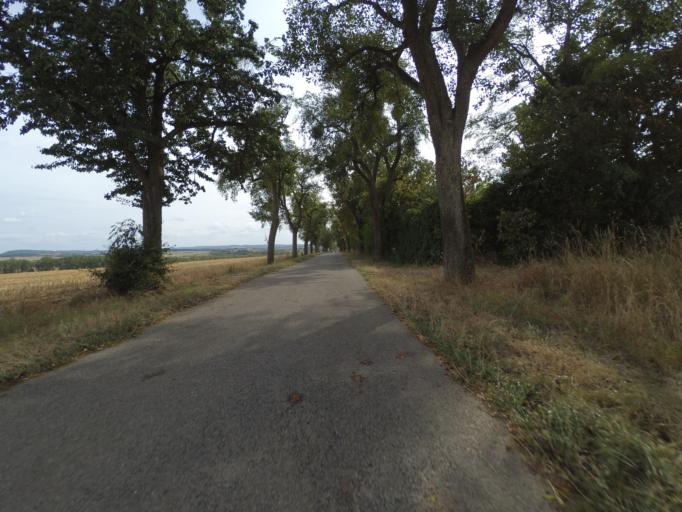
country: LU
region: Grevenmacher
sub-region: Canton de Remich
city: Mondorf-les-Bains
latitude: 49.4972
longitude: 6.2943
